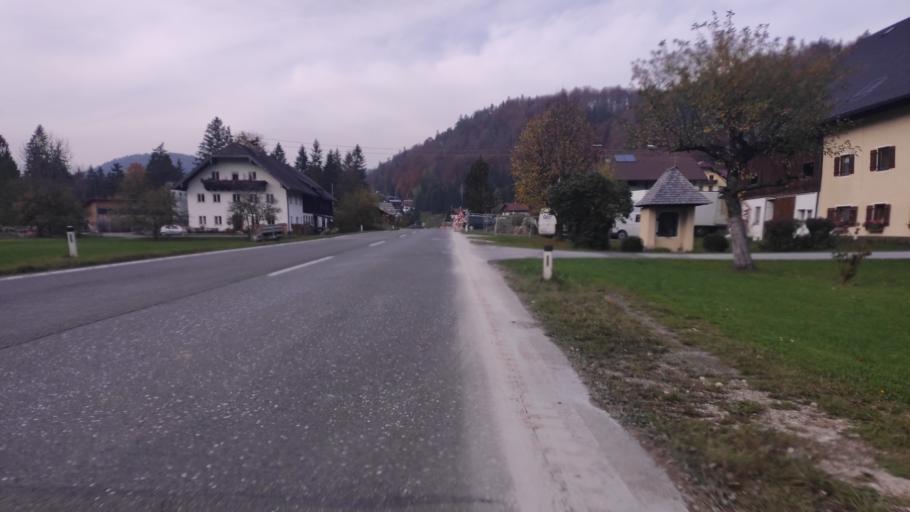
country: AT
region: Salzburg
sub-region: Politischer Bezirk Salzburg-Umgebung
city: Ebenau
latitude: 47.7847
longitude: 13.1787
